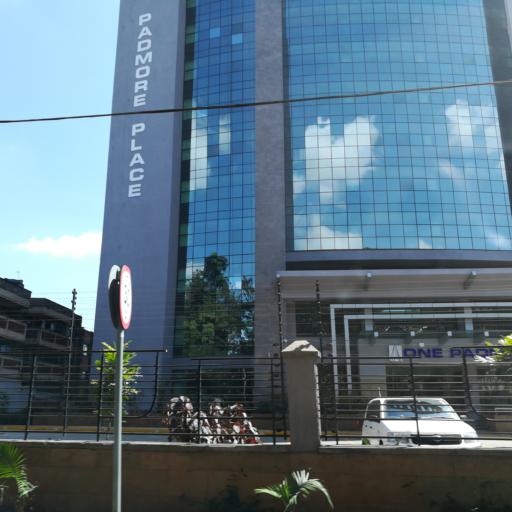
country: KE
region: Nairobi Area
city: Nairobi
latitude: -1.2963
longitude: 36.7923
